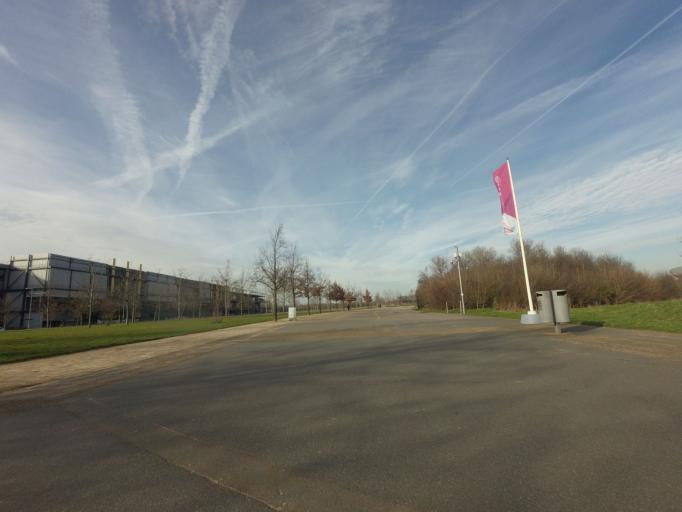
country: GB
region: England
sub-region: Greater London
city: Hackney
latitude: 51.5465
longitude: -0.0187
